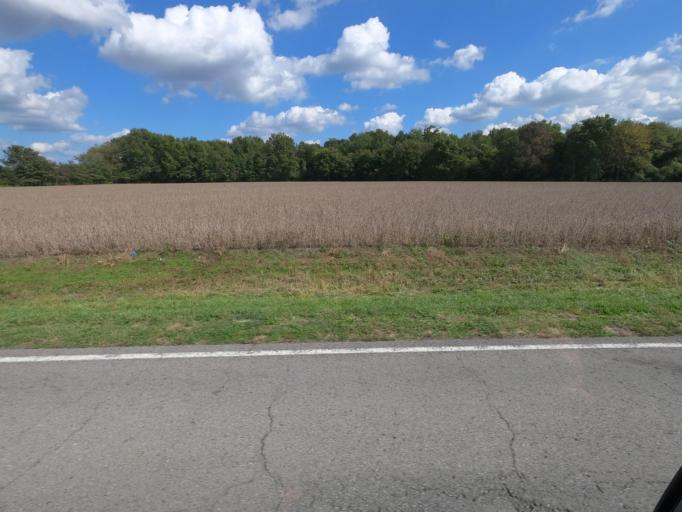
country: US
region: Illinois
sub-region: Massac County
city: Metropolis
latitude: 37.2931
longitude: -88.7563
